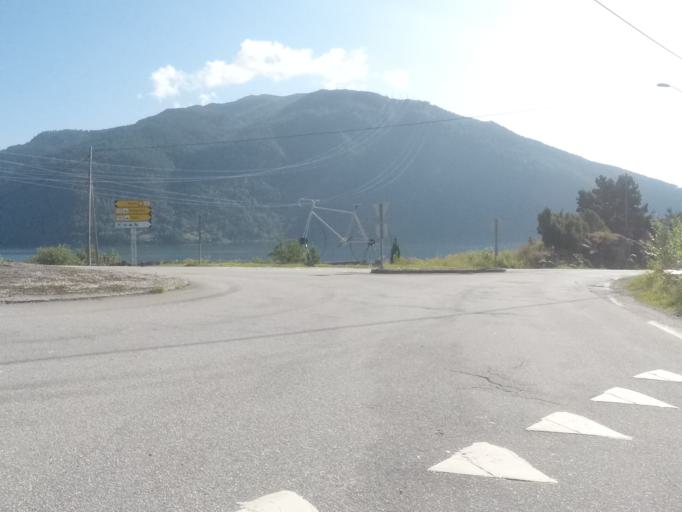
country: NO
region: Sogn og Fjordane
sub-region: Balestrand
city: Balestrand
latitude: 61.2170
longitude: 6.5583
